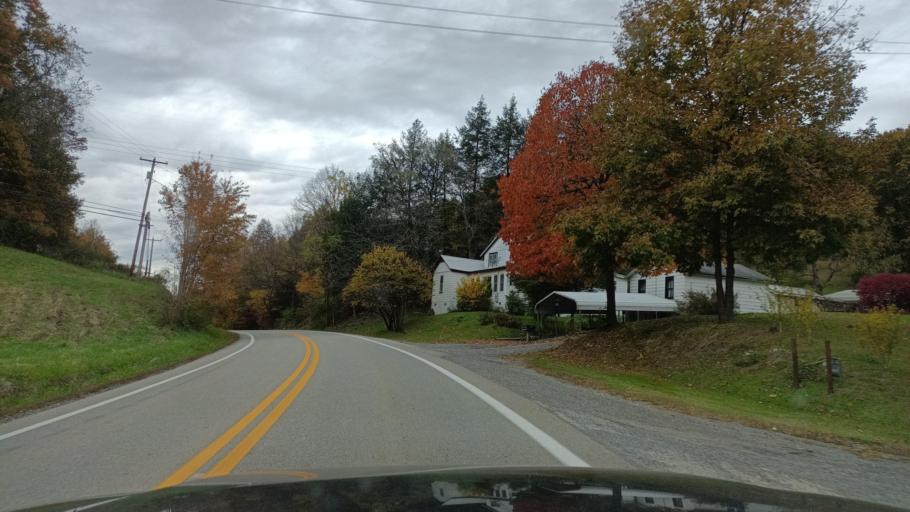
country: US
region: West Virginia
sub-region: Taylor County
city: Grafton
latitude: 39.3553
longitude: -79.9926
